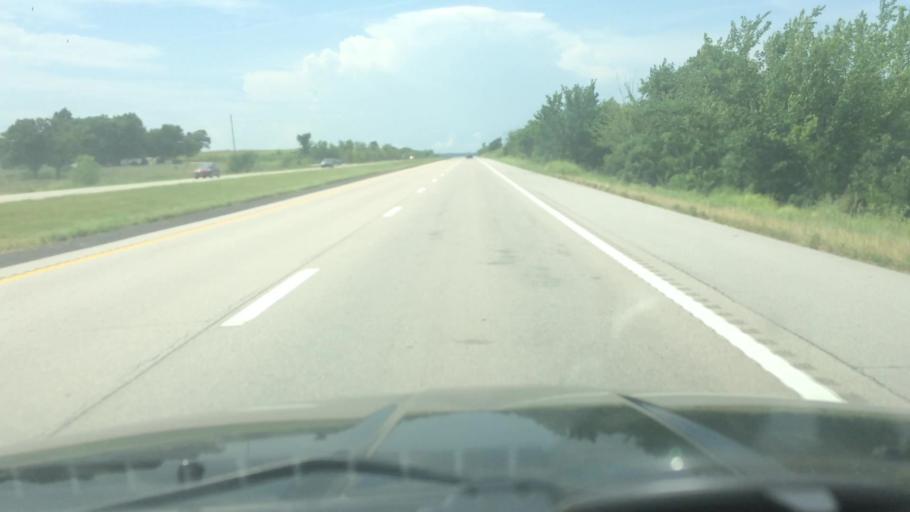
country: US
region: Missouri
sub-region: Polk County
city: Humansville
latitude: 37.7981
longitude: -93.5923
